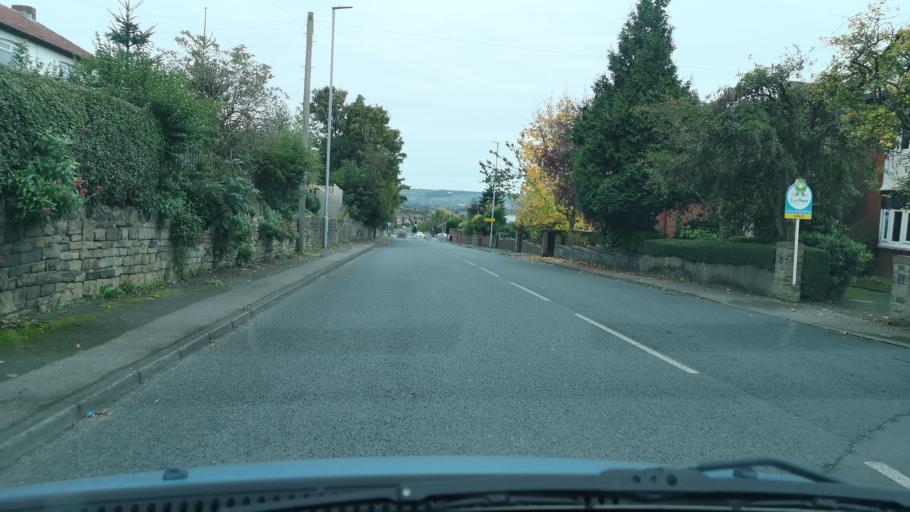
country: GB
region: England
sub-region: Kirklees
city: Heckmondwike
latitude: 53.7173
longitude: -1.6803
